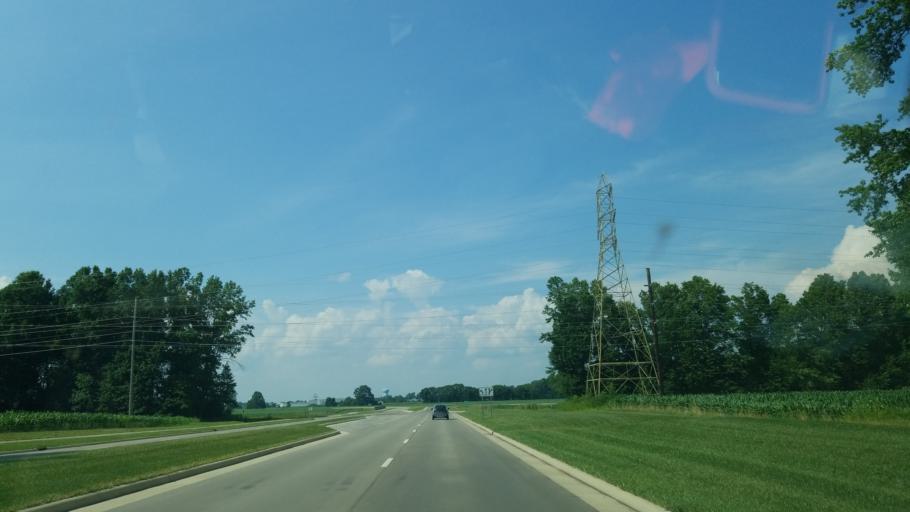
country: US
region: Ohio
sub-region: Delaware County
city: Delaware
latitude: 40.2599
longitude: -83.0912
